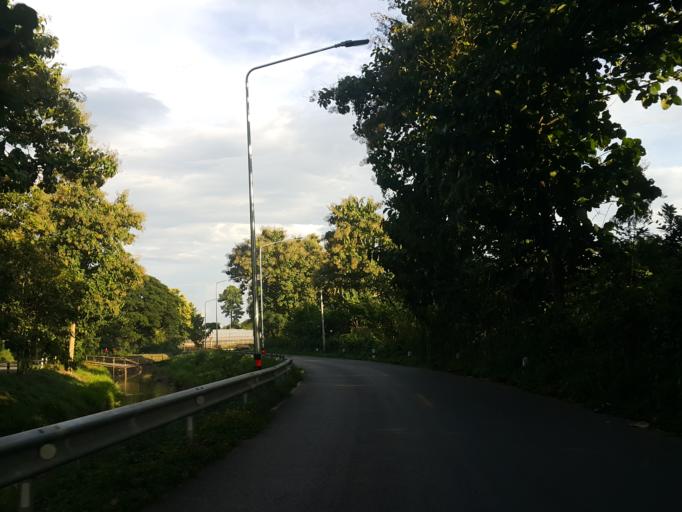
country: TH
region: Chiang Mai
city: San Sai
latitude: 18.9083
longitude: 99.0125
